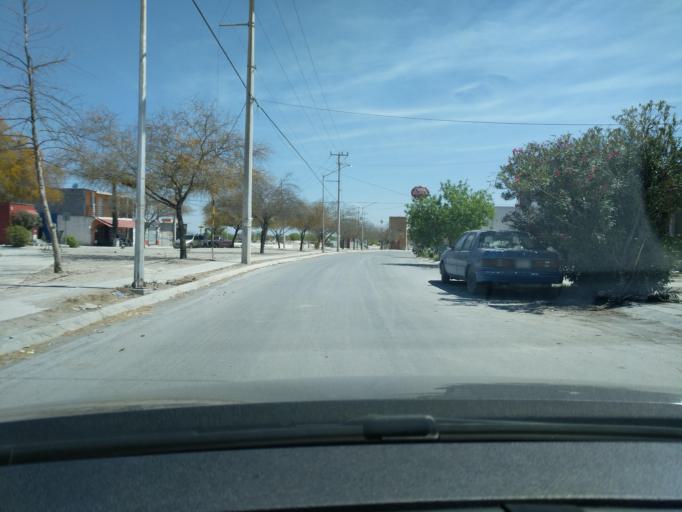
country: MX
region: Nuevo Leon
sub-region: Salinas Victoria
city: Las Torres
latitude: 25.9646
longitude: -100.3066
